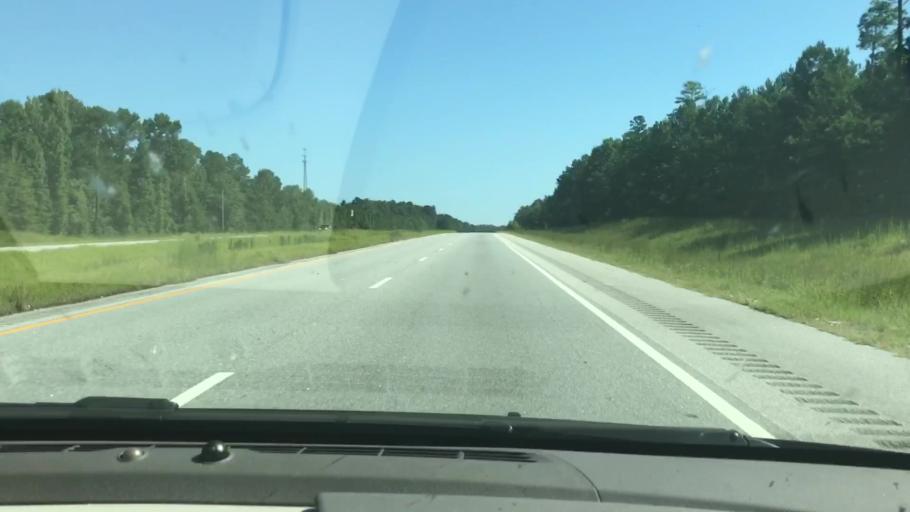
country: US
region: Alabama
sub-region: Russell County
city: Ladonia
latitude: 32.3828
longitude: -85.0821
